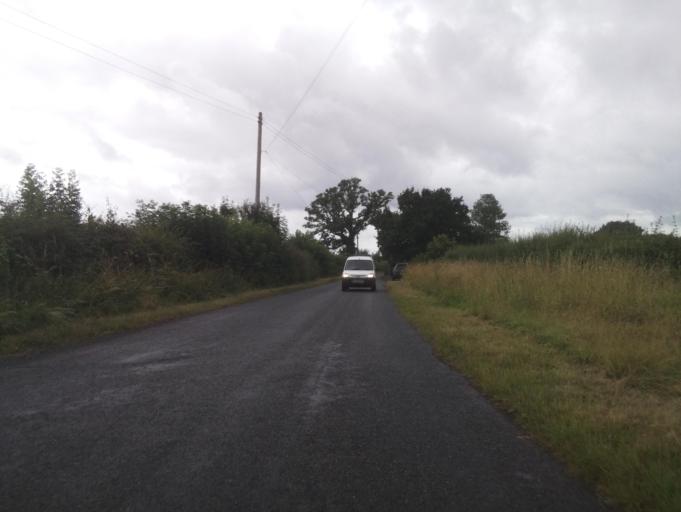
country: GB
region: England
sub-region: Worcestershire
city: Pershore
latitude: 52.1742
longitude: -2.1255
